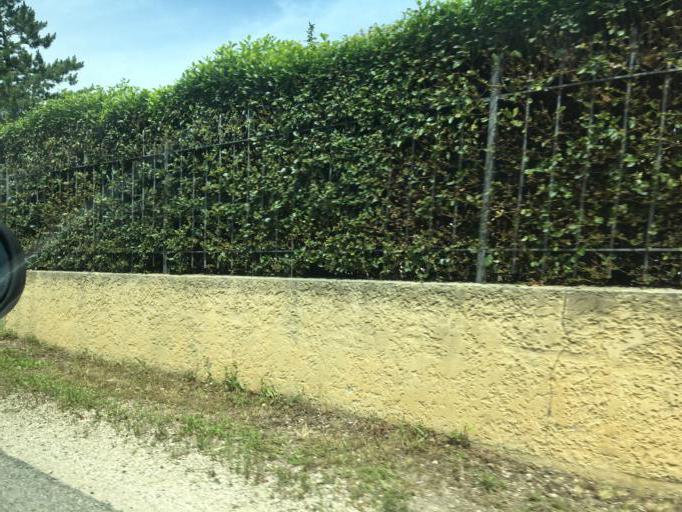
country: FR
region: Provence-Alpes-Cote d'Azur
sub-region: Departement du Vaucluse
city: Camaret-sur-Aigues
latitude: 44.1576
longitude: 4.8667
